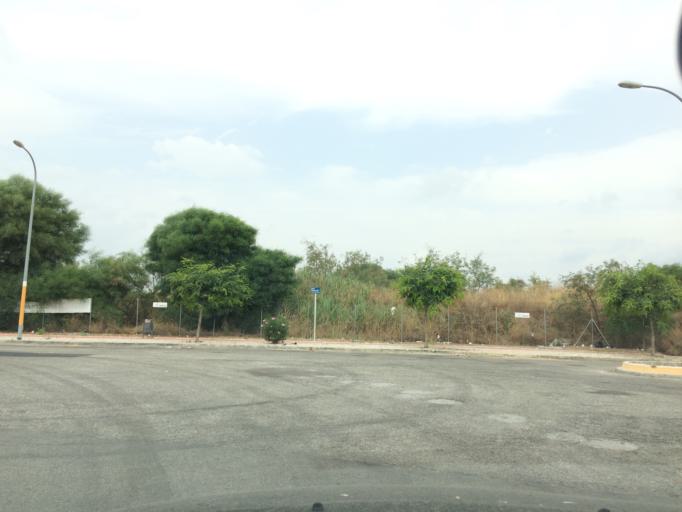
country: ES
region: Andalusia
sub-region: Provincia de Malaga
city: Malaga
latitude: 36.6984
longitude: -4.4829
